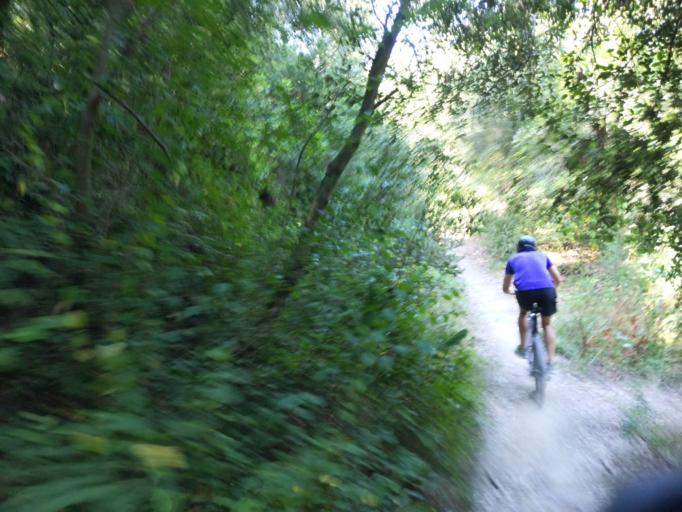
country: ES
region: Catalonia
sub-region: Provincia de Barcelona
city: Nou Barris
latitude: 41.4609
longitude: 2.1522
